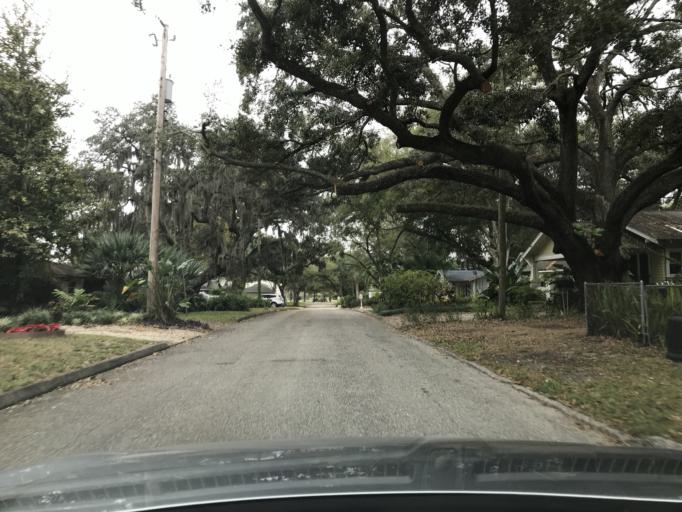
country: US
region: Florida
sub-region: Hillsborough County
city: Tampa
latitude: 27.9922
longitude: -82.4635
